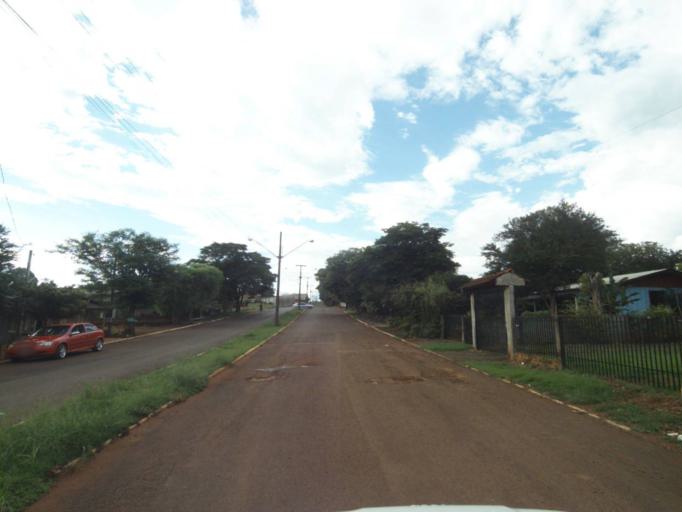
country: BR
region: Parana
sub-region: Laranjeiras Do Sul
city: Laranjeiras do Sul
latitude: -25.4953
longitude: -52.5269
